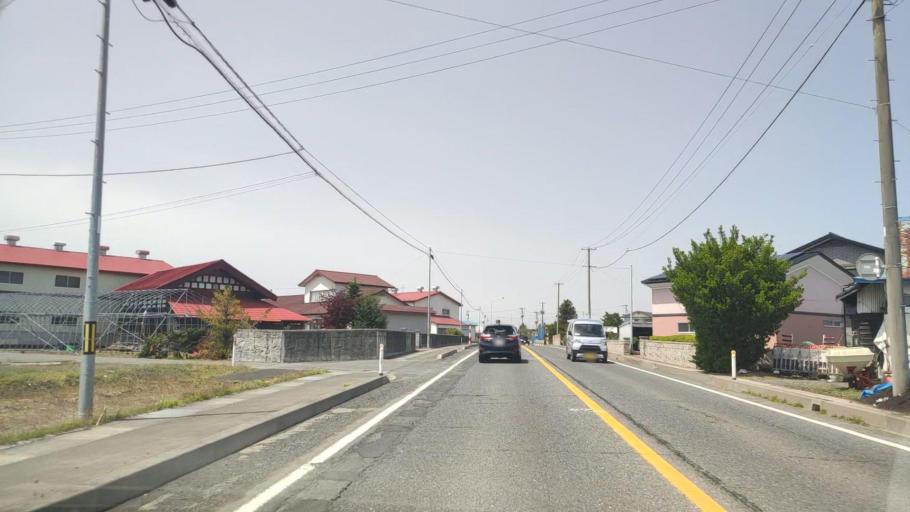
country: JP
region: Aomori
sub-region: Misawa Shi
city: Inuotose
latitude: 40.6082
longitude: 141.2857
